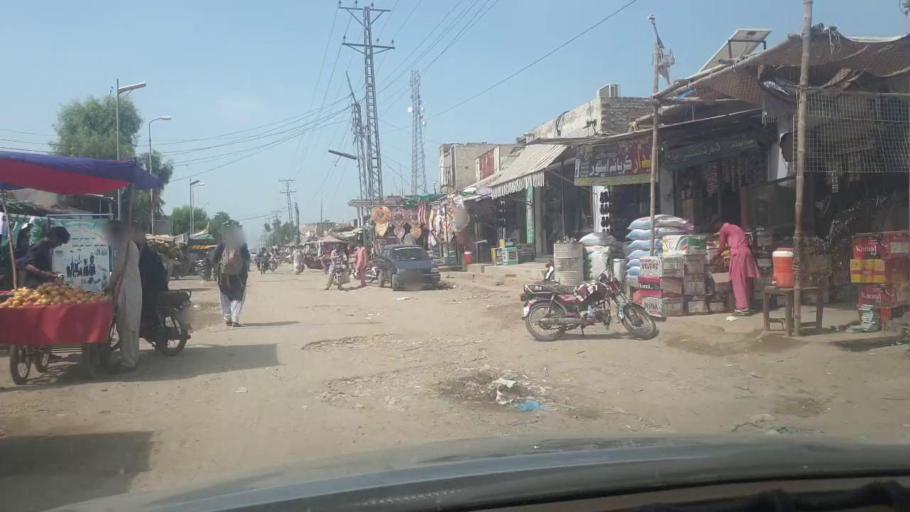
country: PK
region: Sindh
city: Gambat
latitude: 27.3013
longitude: 68.6117
